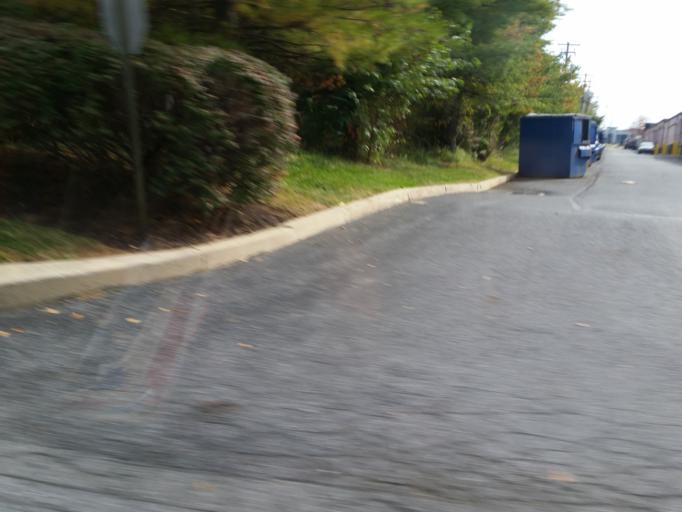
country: US
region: Pennsylvania
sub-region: Lancaster County
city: East Petersburg
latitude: 40.0765
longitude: -76.3219
